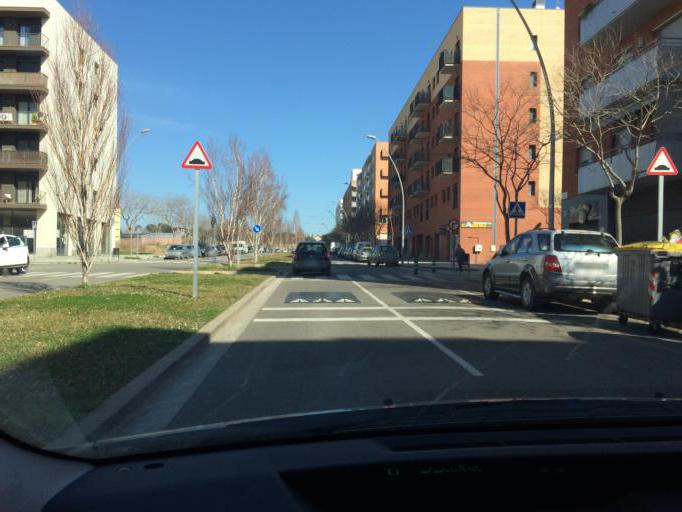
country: ES
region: Catalonia
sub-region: Provincia de Barcelona
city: Manresa
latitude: 41.7394
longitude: 1.8386
